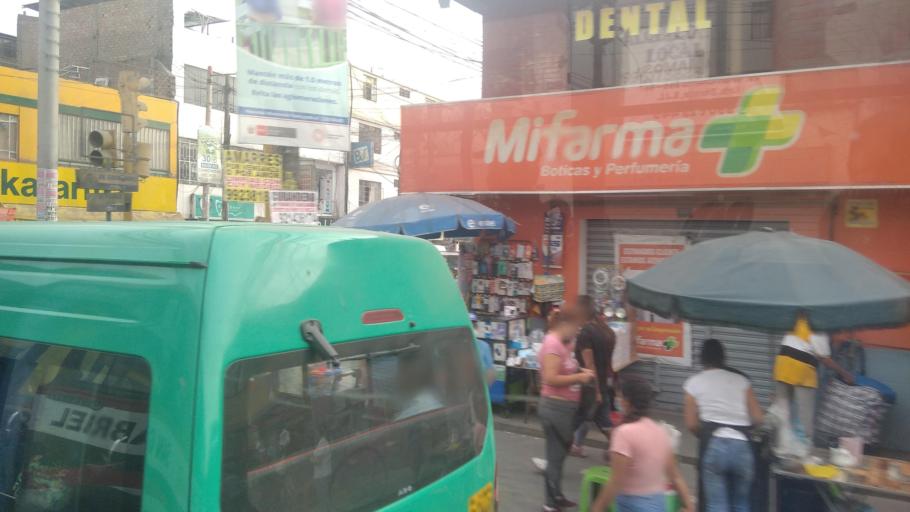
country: PE
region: Lima
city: Lima
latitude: -12.0255
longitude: -77.0020
